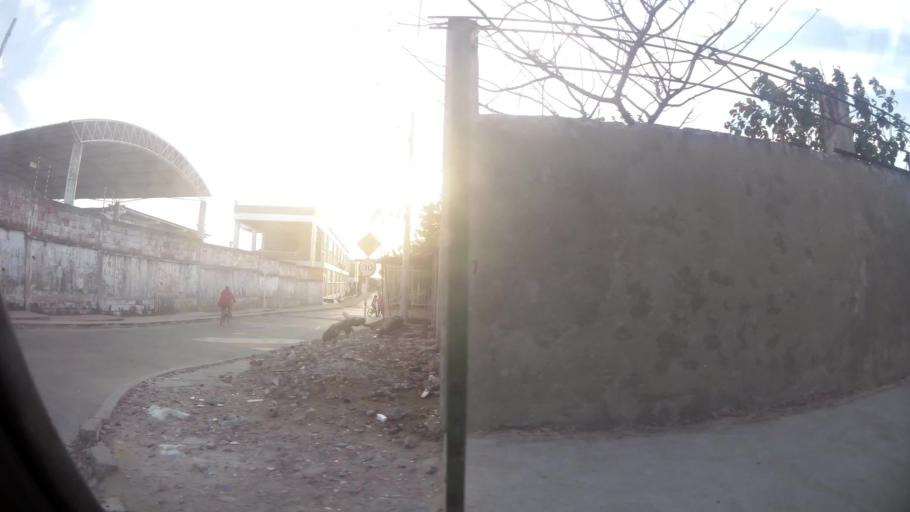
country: CO
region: Atlantico
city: Barranquilla
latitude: 10.9541
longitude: -74.8281
